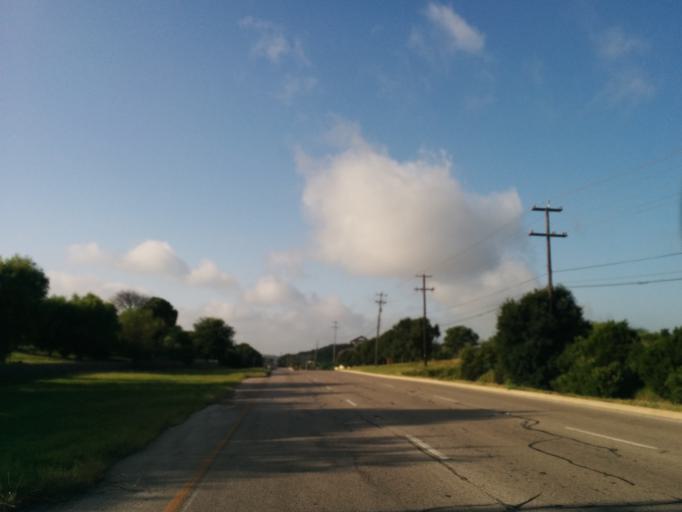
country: US
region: Texas
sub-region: Bexar County
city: Shavano Park
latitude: 29.6081
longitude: -98.6032
